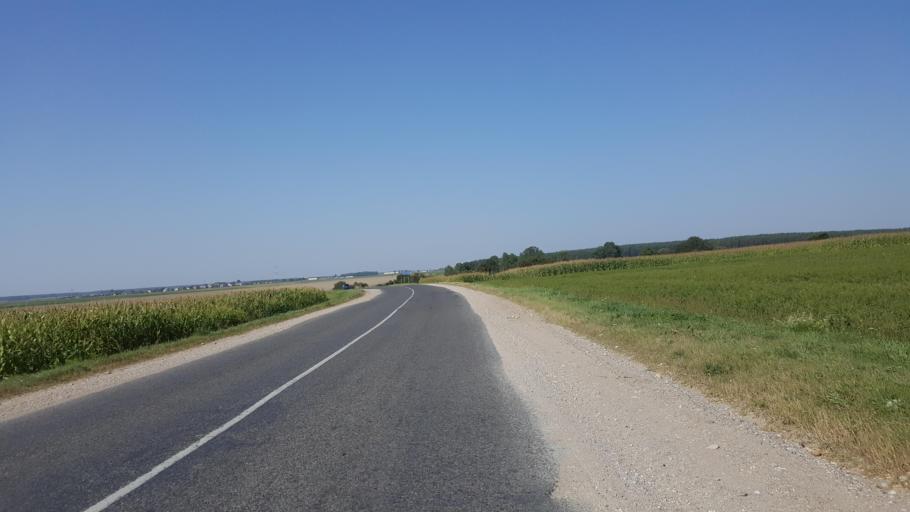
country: BY
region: Brest
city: Kamyanyets
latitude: 52.4178
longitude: 23.6702
